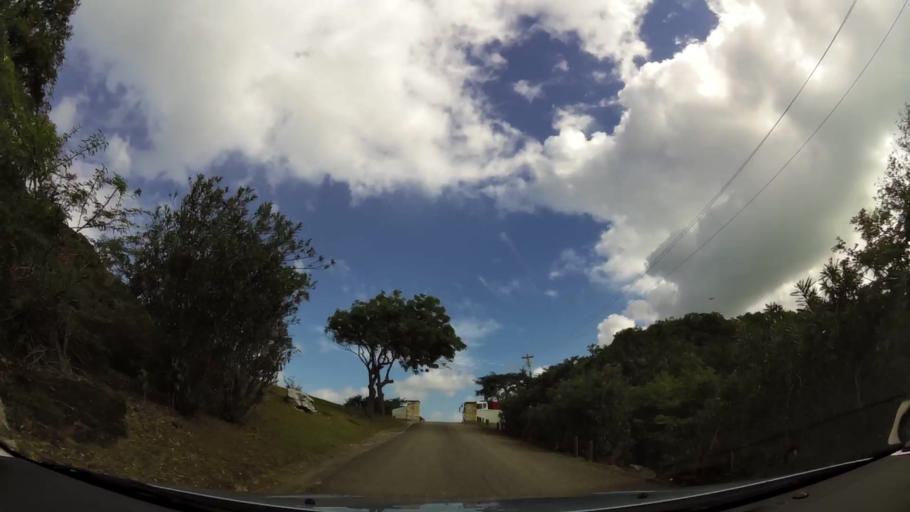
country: AG
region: Saint John
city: Saint John's
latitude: 17.1188
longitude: -61.8956
